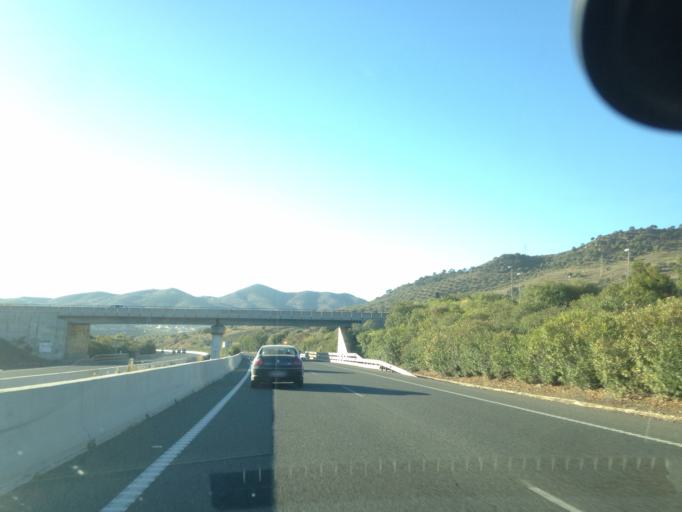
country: ES
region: Andalusia
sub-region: Provincia de Malaga
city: Casabermeja
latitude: 36.9252
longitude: -4.4473
